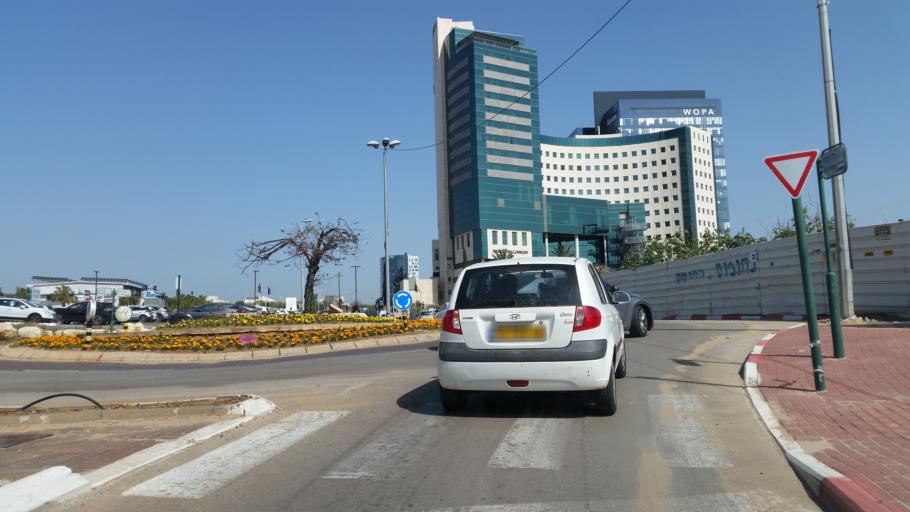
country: IL
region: Central District
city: Ra'anana
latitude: 32.1930
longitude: 34.8825
